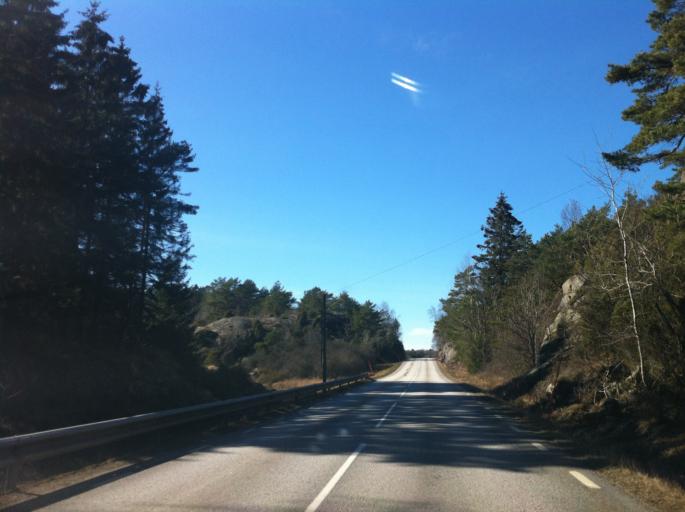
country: SE
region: Vaestra Goetaland
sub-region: Sotenas Kommun
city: Hunnebostrand
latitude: 58.4141
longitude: 11.3680
